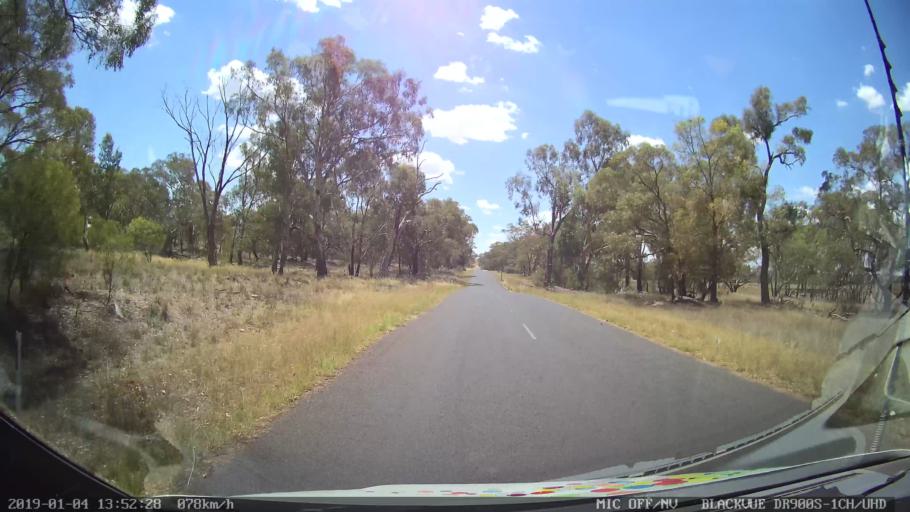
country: AU
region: New South Wales
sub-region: Dubbo Municipality
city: Dubbo
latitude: -32.3939
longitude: 148.5715
